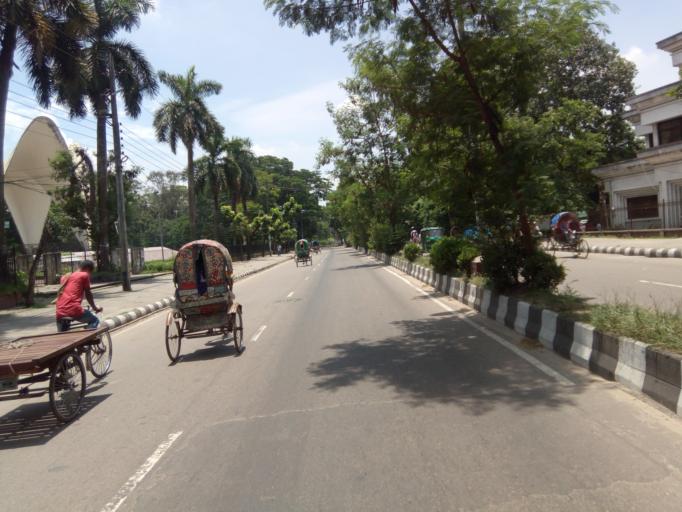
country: BD
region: Dhaka
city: Azimpur
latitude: 23.7292
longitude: 90.3991
